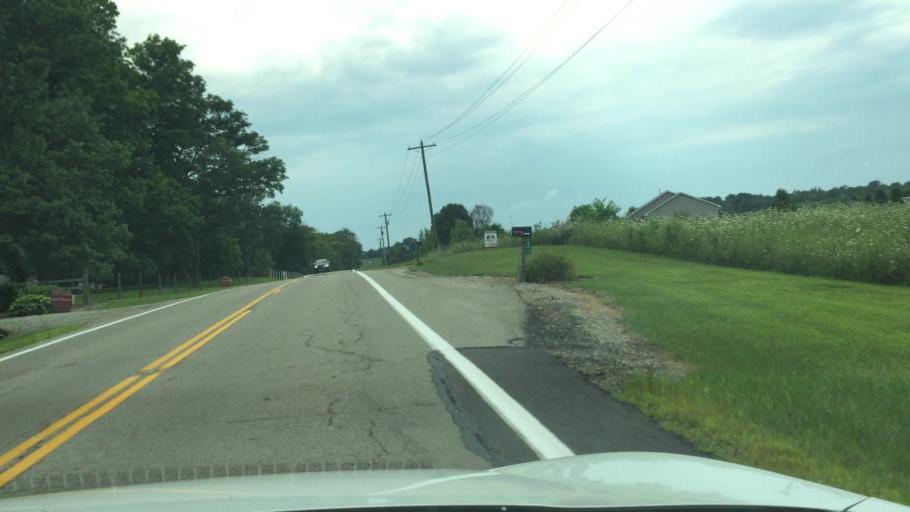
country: US
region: Ohio
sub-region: Champaign County
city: Mechanicsburg
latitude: 40.1006
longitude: -83.5637
